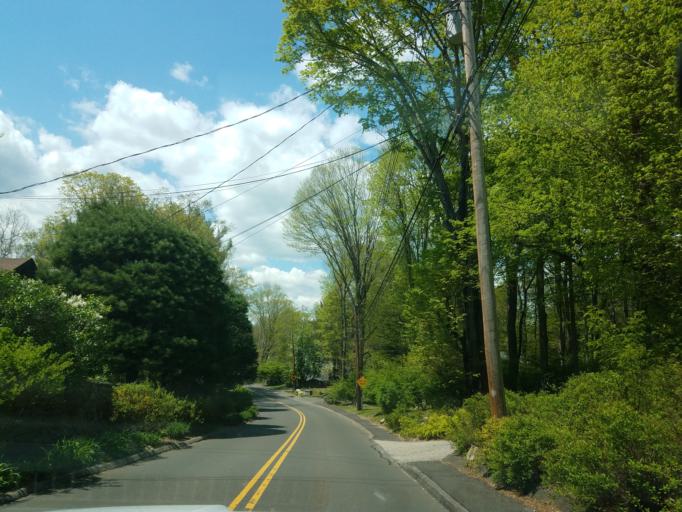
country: US
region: Connecticut
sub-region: Fairfield County
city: Wilton
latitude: 41.1508
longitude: -73.4436
